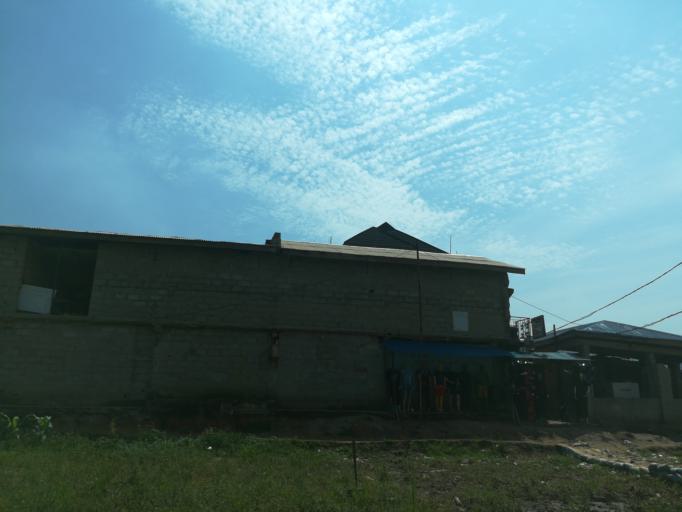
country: NG
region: Lagos
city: Ikorodu
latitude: 6.6447
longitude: 3.4798
